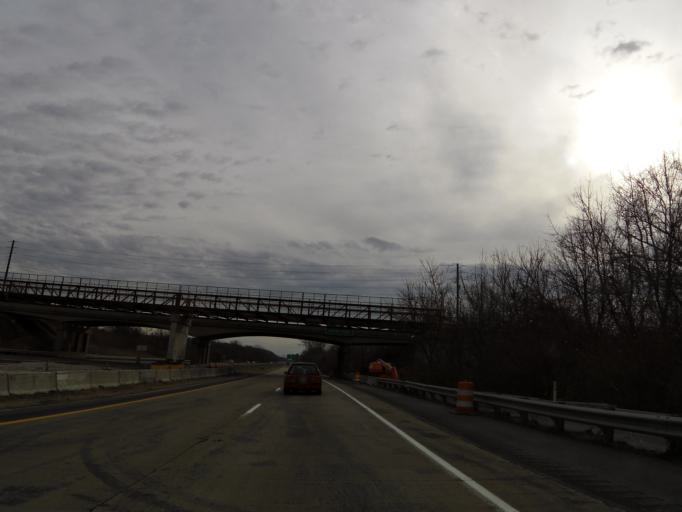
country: US
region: Indiana
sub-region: Marion County
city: Clermont
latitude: 39.8171
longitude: -86.3011
